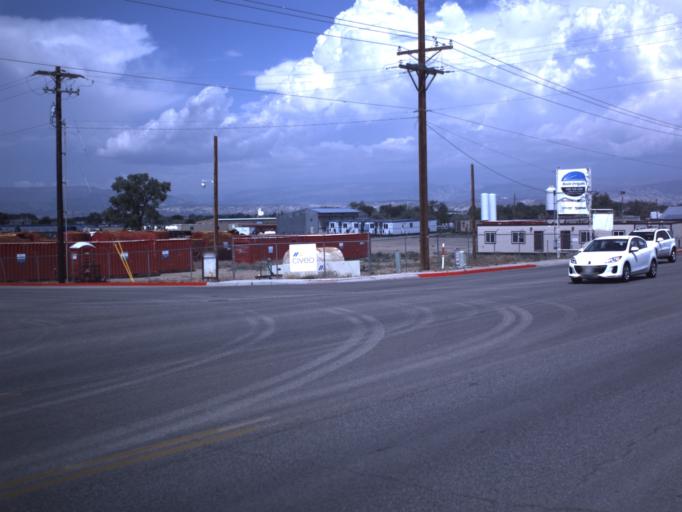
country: US
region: Utah
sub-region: Uintah County
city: Naples
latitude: 40.4265
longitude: -109.4993
